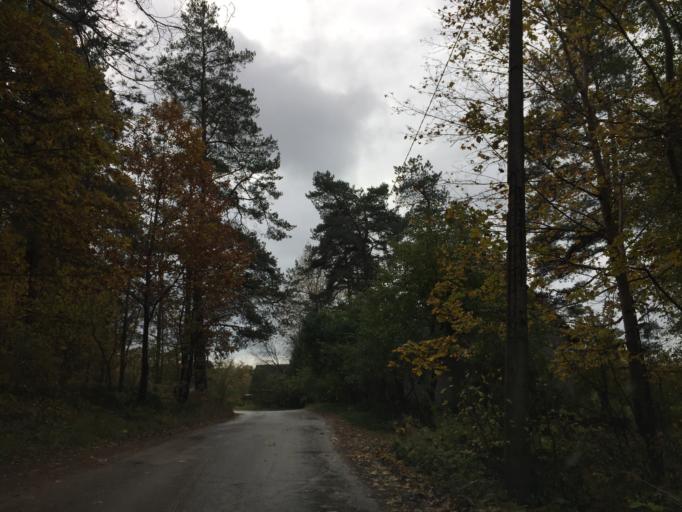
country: LV
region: Ogre
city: Ogre
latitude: 56.7971
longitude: 24.6404
